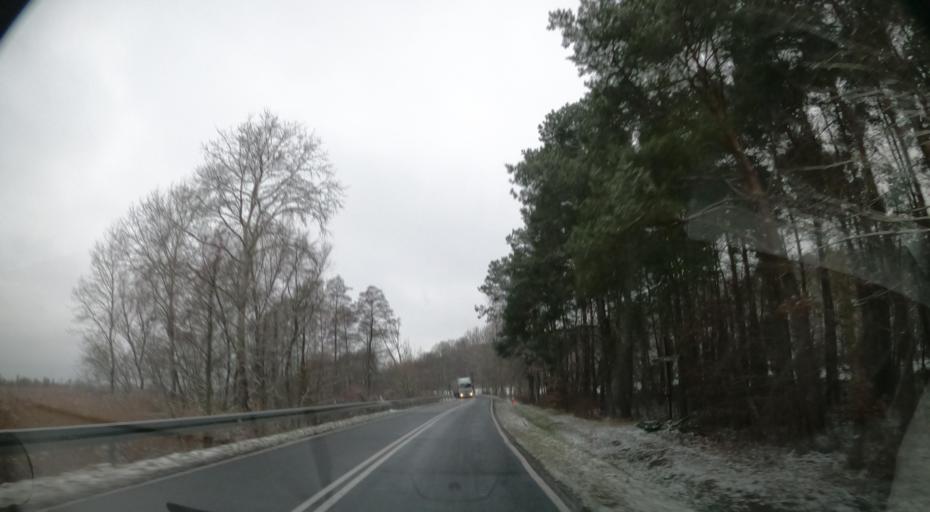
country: PL
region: Masovian Voivodeship
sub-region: Powiat plocki
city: Nowy Duninow
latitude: 52.5763
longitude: 19.5491
